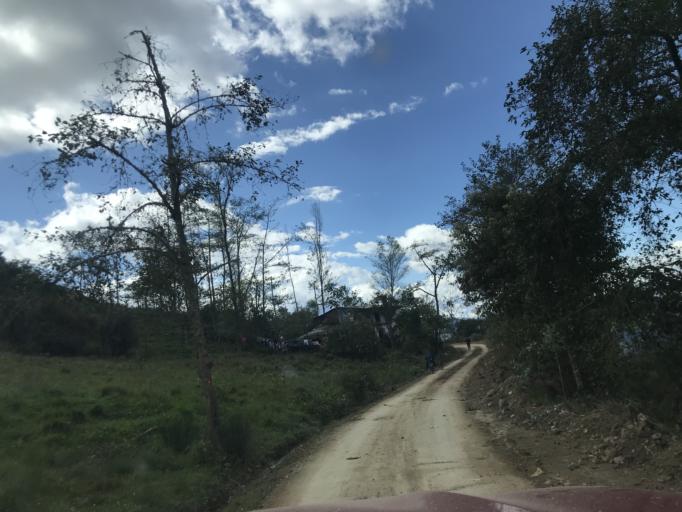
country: PE
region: Cajamarca
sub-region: Provincia de Chota
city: Querocoto
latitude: -6.3393
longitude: -79.0649
